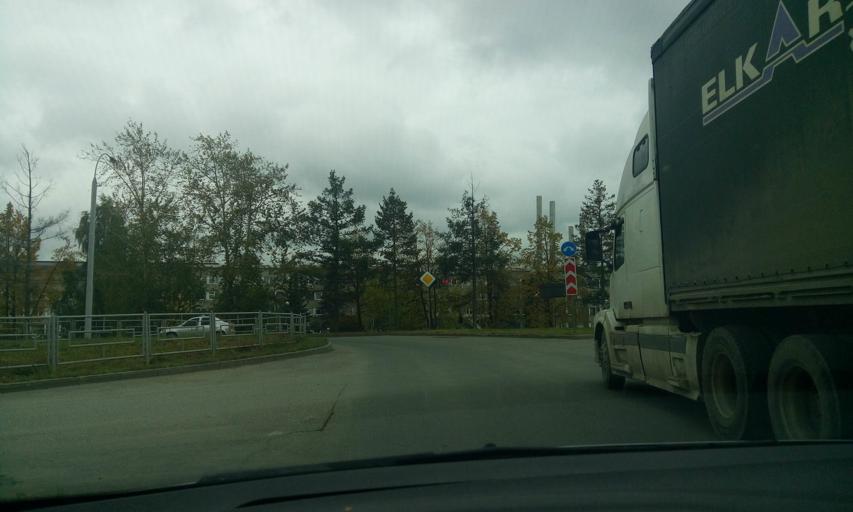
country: RU
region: Sverdlovsk
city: Yekaterinburg
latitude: 56.8520
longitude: 60.5494
